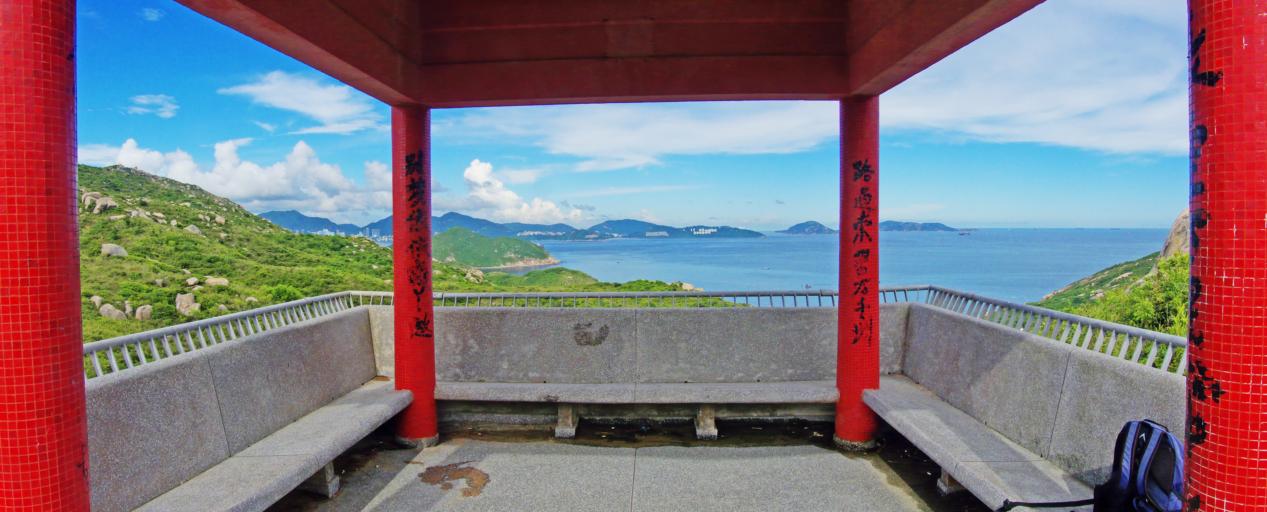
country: HK
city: Sok Kwu Wan
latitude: 22.1978
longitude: 114.1349
